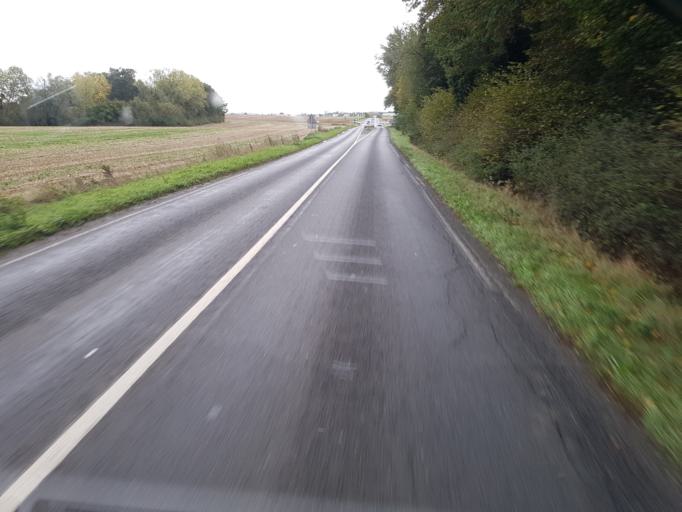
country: FR
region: Ile-de-France
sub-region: Departement de Seine-et-Marne
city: Saint-Pathus
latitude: 49.0554
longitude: 2.7840
